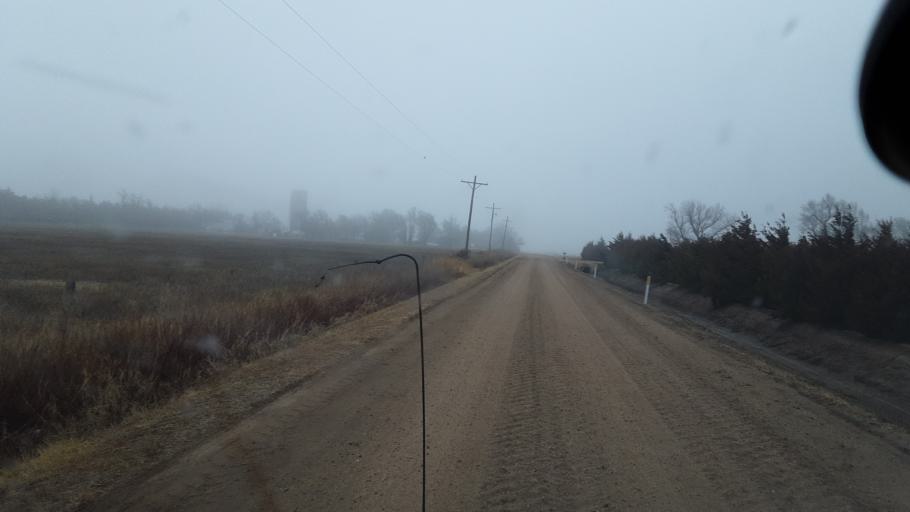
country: US
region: Kansas
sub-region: Reno County
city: South Hutchinson
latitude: 37.9844
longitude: -97.9938
